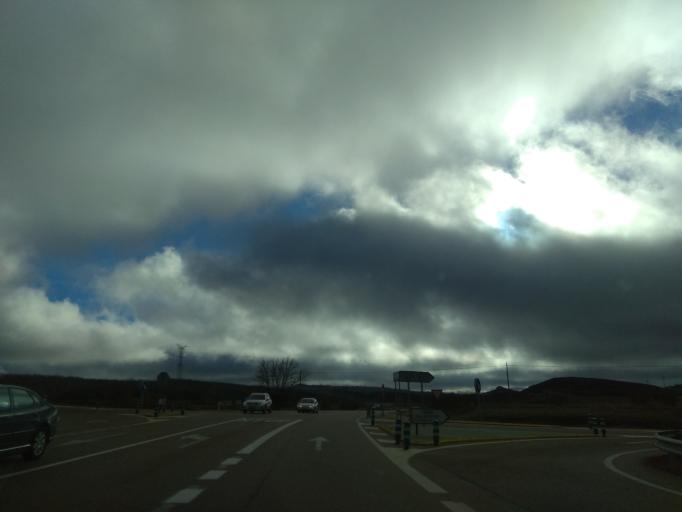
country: ES
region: Castille and Leon
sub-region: Provincia de Burgos
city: Montorio
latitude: 42.6029
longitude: -3.7963
